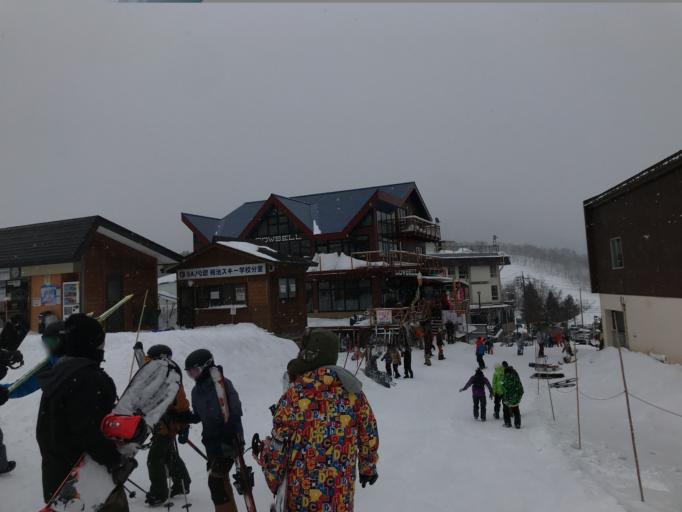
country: JP
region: Nagano
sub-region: Kitaazumi Gun
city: Hakuba
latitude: 36.7498
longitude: 137.8708
